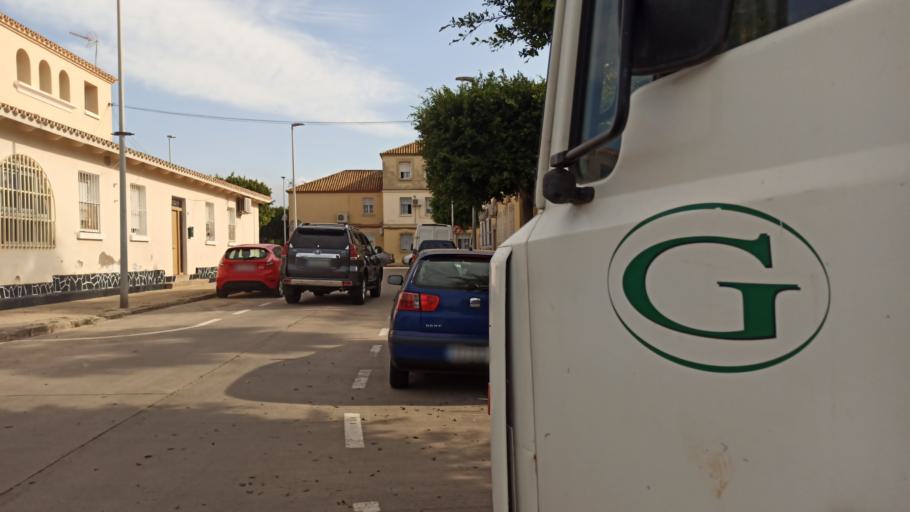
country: ES
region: Melilla
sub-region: Melilla
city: Melilla
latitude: 35.2887
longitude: -2.9509
